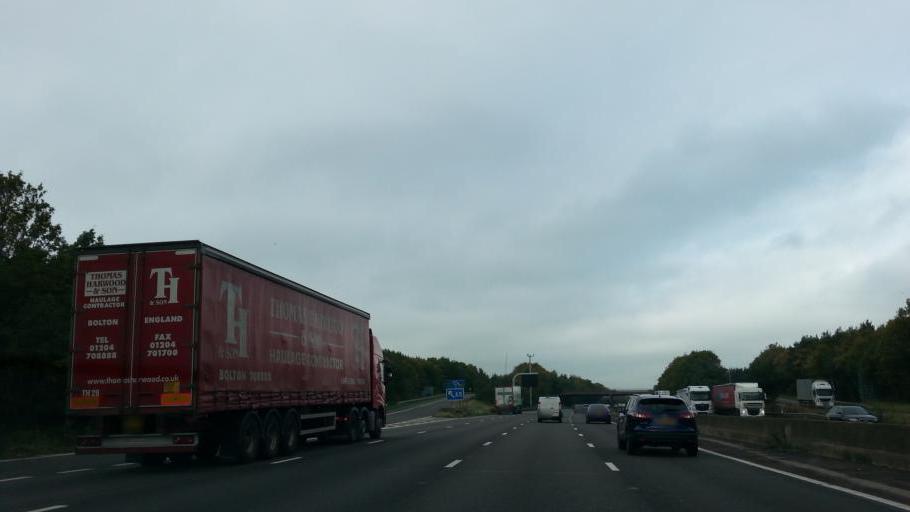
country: GB
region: England
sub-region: Staffordshire
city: Featherstone
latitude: 52.6857
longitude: -2.1007
